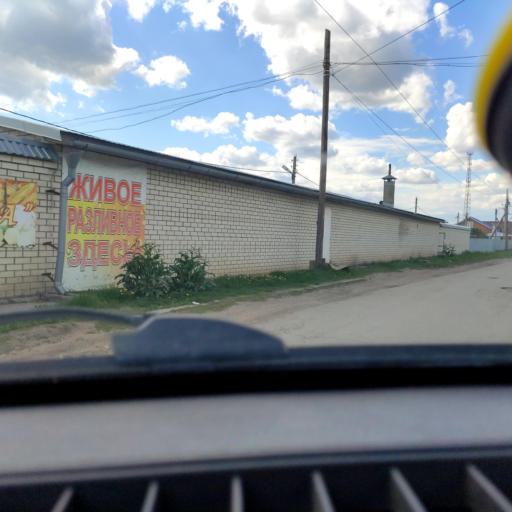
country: RU
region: Samara
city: Povolzhskiy
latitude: 53.6436
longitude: 49.6847
